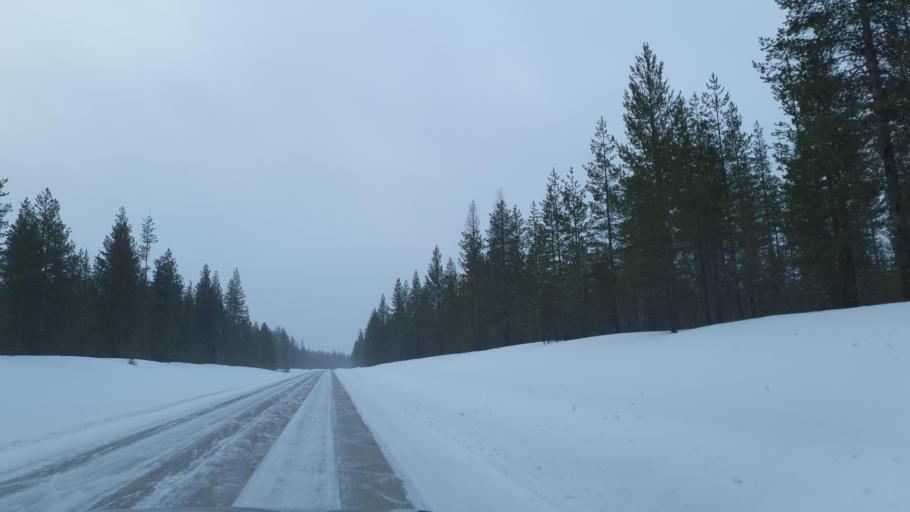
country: FI
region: Lapland
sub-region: Tunturi-Lappi
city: Kolari
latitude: 67.5097
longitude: 23.9031
